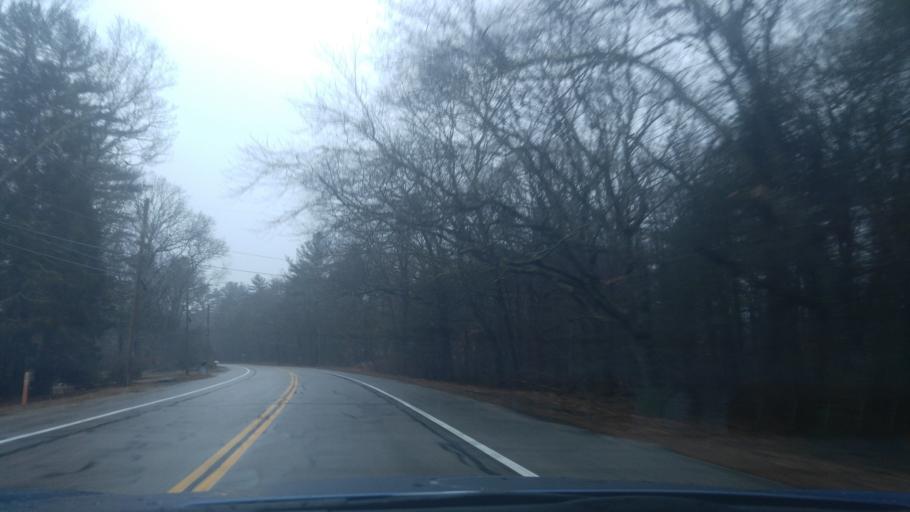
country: US
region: Rhode Island
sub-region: Washington County
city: Charlestown
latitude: 41.4686
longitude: -71.6195
